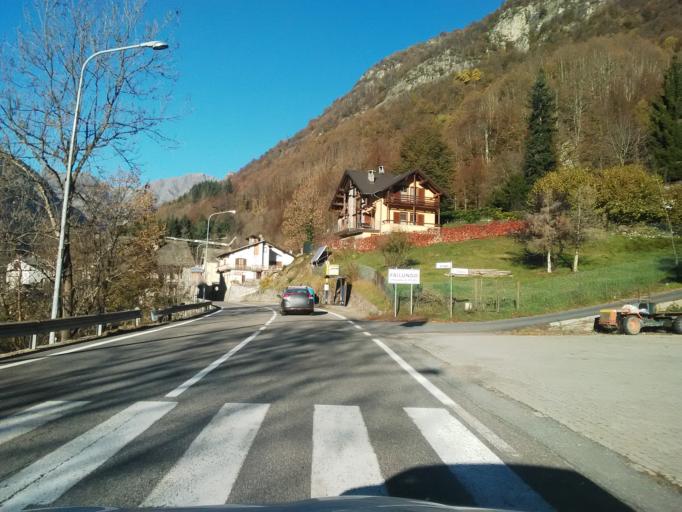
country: IT
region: Piedmont
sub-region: Provincia di Vercelli
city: Pila
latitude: 45.7706
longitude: 8.0743
